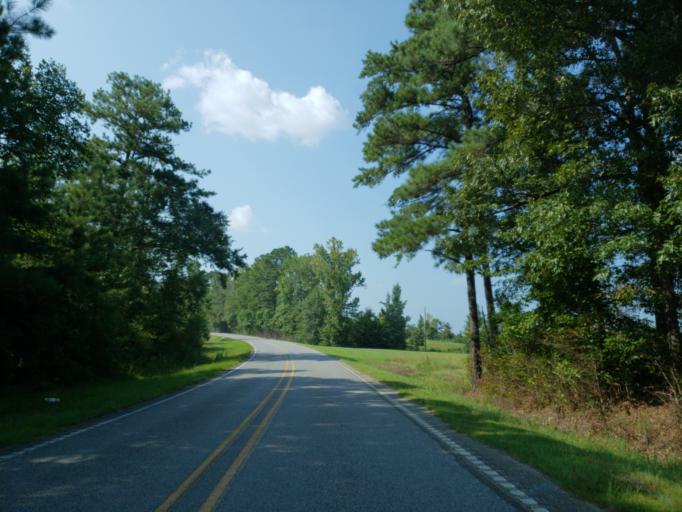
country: US
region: Mississippi
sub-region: Clarke County
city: Stonewall
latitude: 32.1193
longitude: -88.8525
